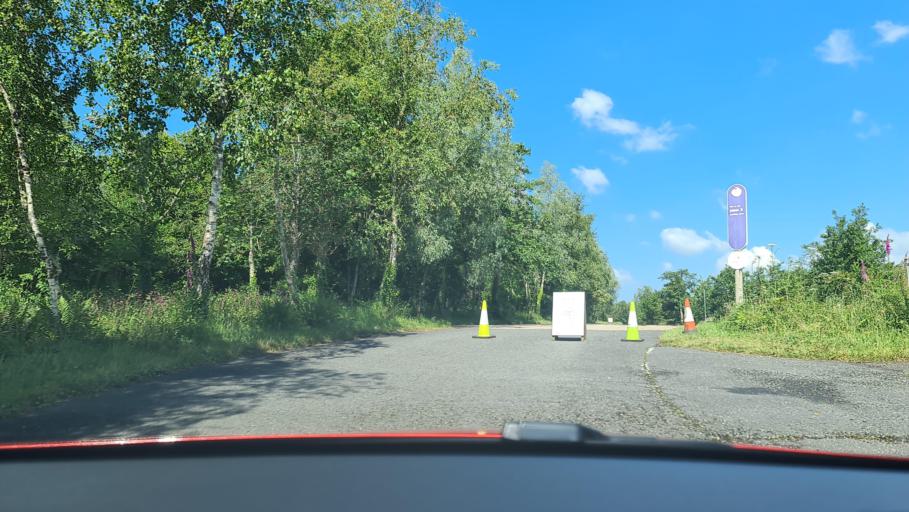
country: GB
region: England
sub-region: Cornwall
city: St Austell
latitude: 50.3578
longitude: -4.7458
